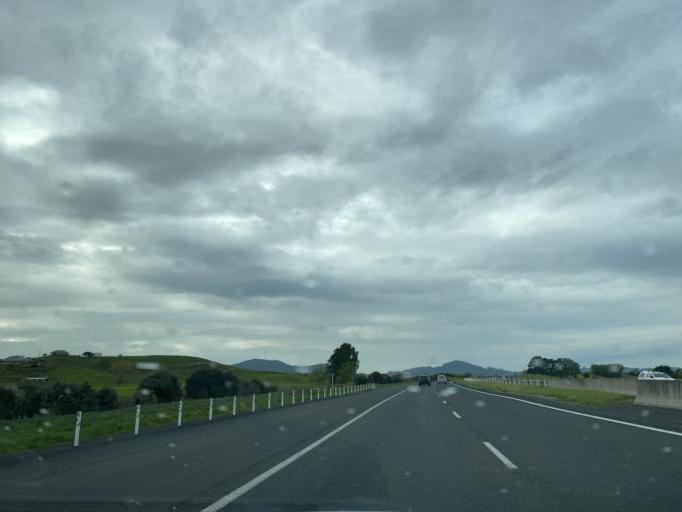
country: NZ
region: Waikato
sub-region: Waikato District
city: Ngaruawahia
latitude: -37.6748
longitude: 175.2090
